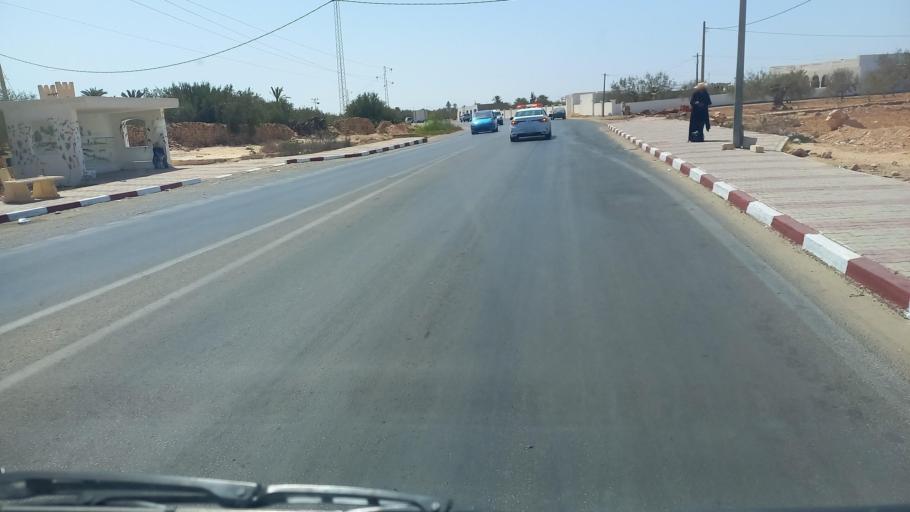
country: TN
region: Madanin
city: Houmt Souk
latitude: 33.8228
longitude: 10.8704
